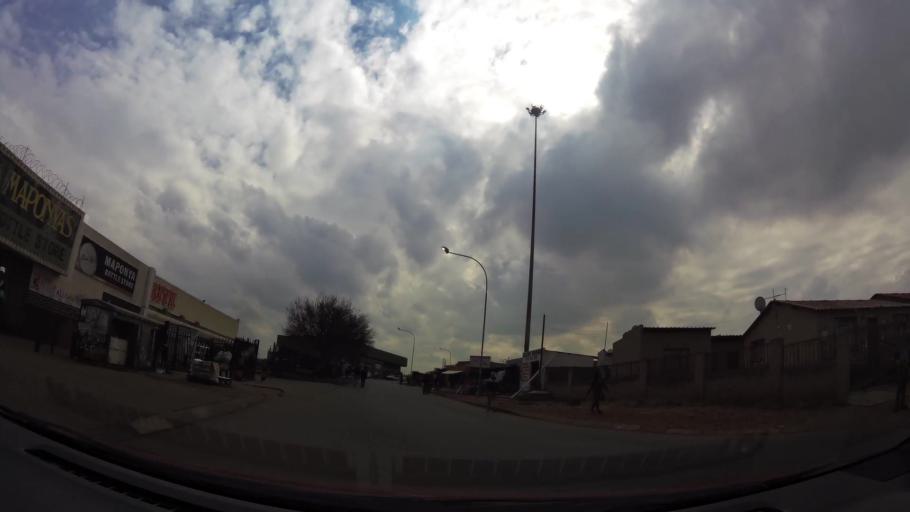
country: ZA
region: Gauteng
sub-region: City of Johannesburg Metropolitan Municipality
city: Soweto
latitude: -26.2561
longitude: 27.8224
